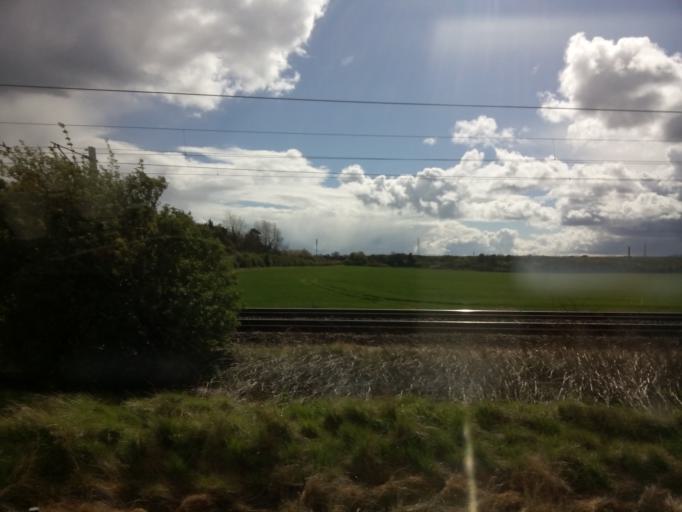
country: GB
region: Scotland
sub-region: East Lothian
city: Musselburgh
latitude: 55.9298
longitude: -3.0625
